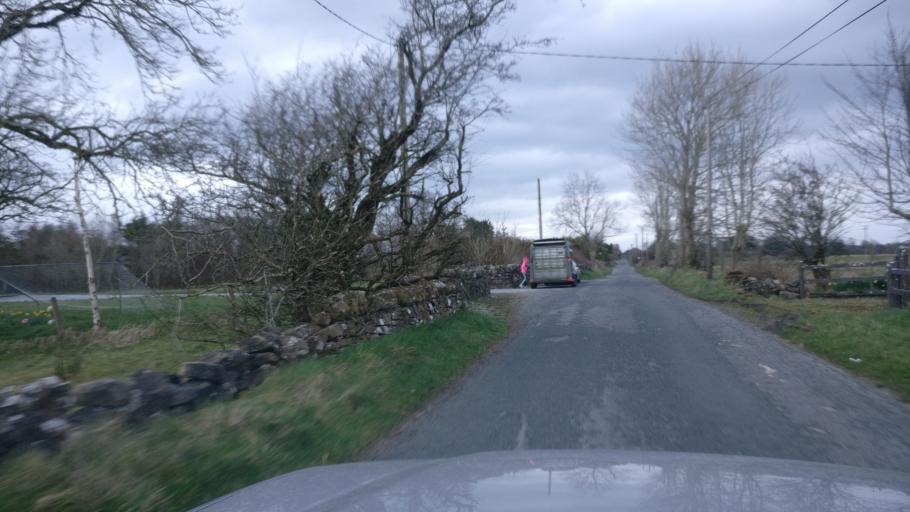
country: IE
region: Connaught
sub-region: County Galway
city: Loughrea
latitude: 53.2586
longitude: -8.5074
